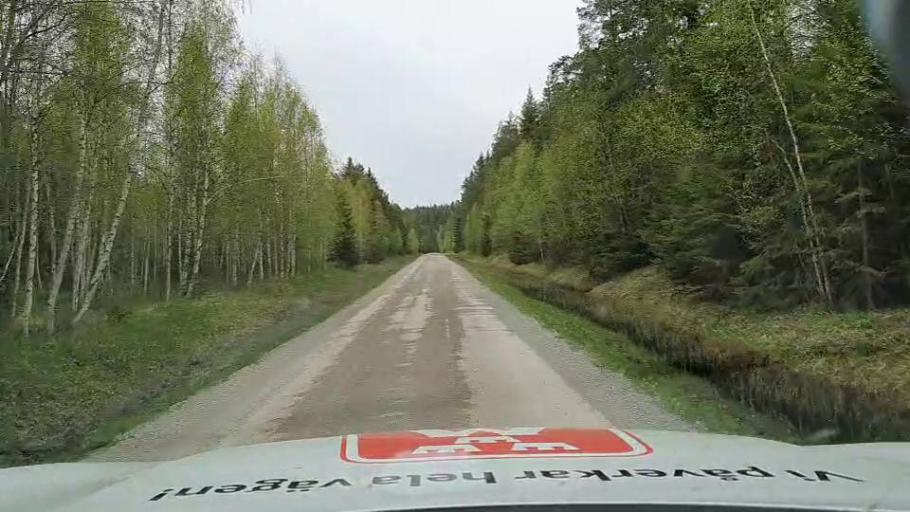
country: SE
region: Jaemtland
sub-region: OEstersunds Kommun
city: Brunflo
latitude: 62.9406
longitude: 14.6655
